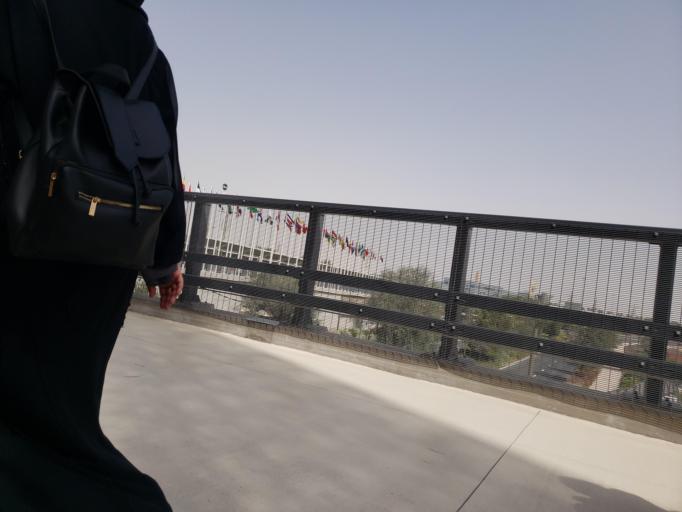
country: AE
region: Dubai
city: Dubai
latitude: 24.9677
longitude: 55.1534
